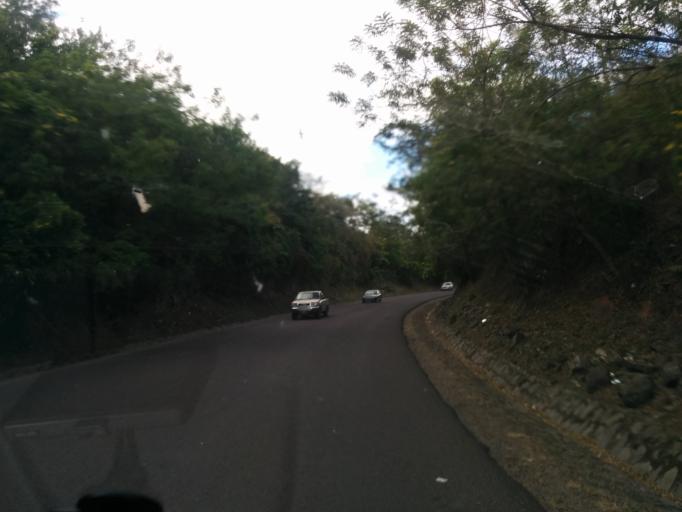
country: NI
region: Esteli
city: Esteli
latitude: 13.1784
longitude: -86.3690
